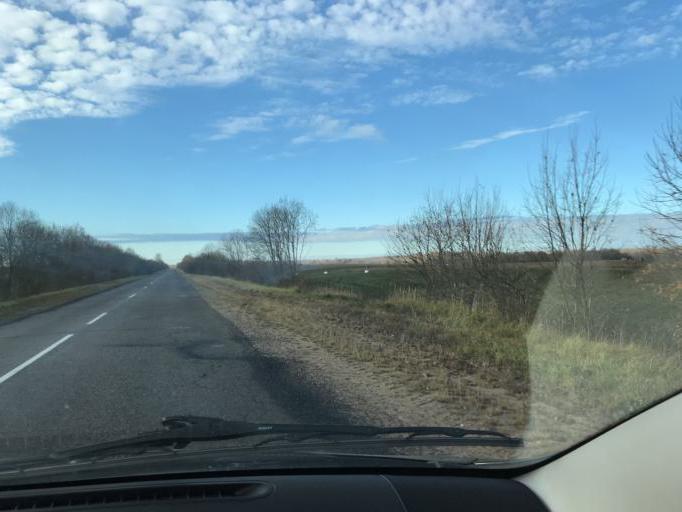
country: BY
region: Vitebsk
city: Haradok
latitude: 55.4100
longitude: 29.7524
